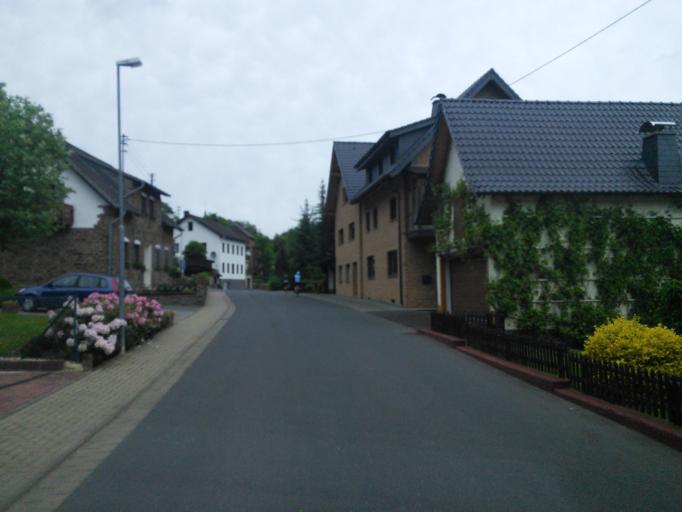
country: DE
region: Rheinland-Pfalz
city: Kirchsahr
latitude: 50.5210
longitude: 6.8986
